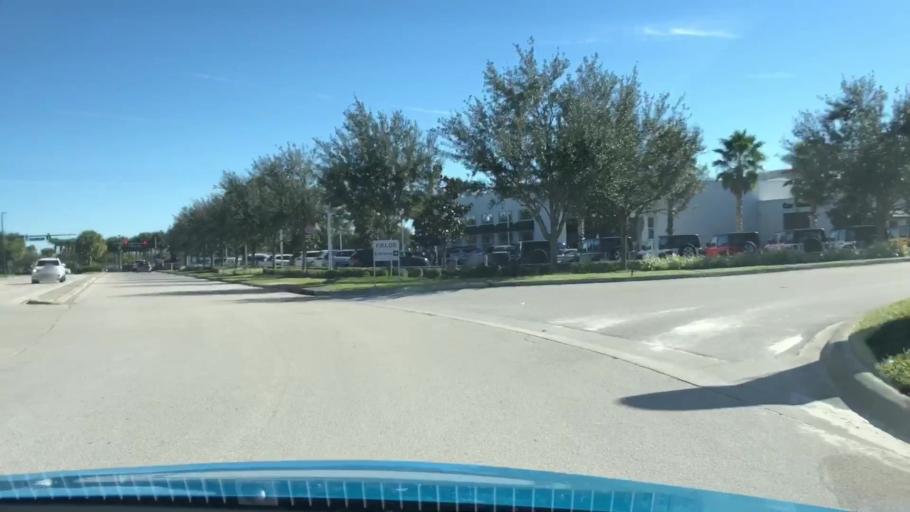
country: US
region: Florida
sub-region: Seminole County
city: Lake Mary
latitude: 28.7994
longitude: -81.3410
